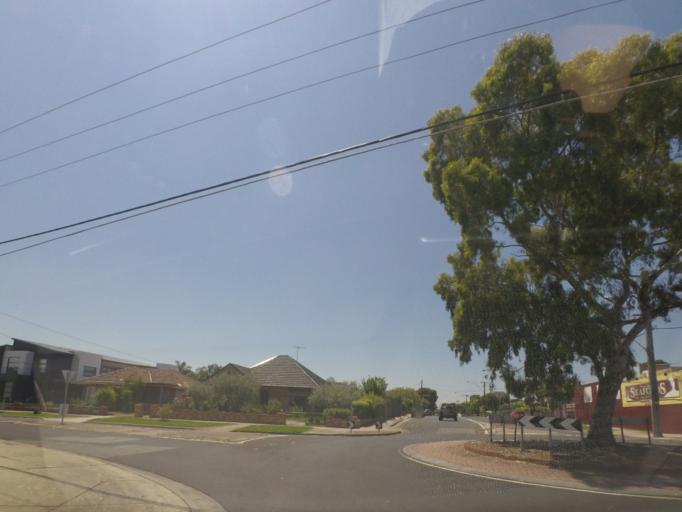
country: AU
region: Victoria
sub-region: Moreland
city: Hadfield
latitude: -37.7202
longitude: 144.9402
